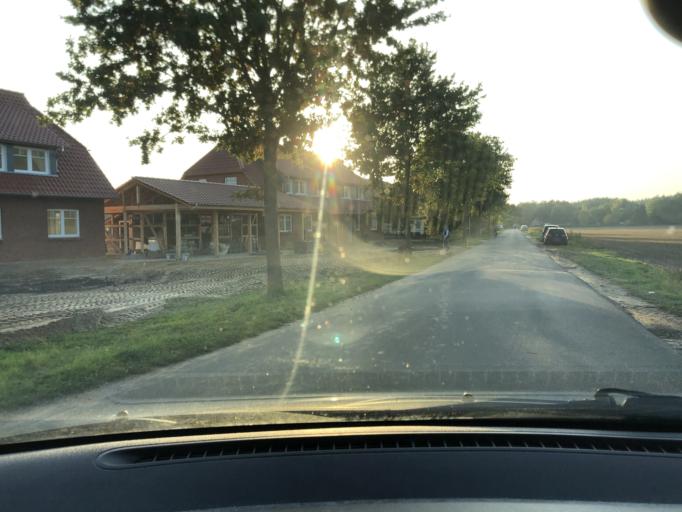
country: DE
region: Lower Saxony
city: Hitzacker
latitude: 53.1526
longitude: 11.0042
